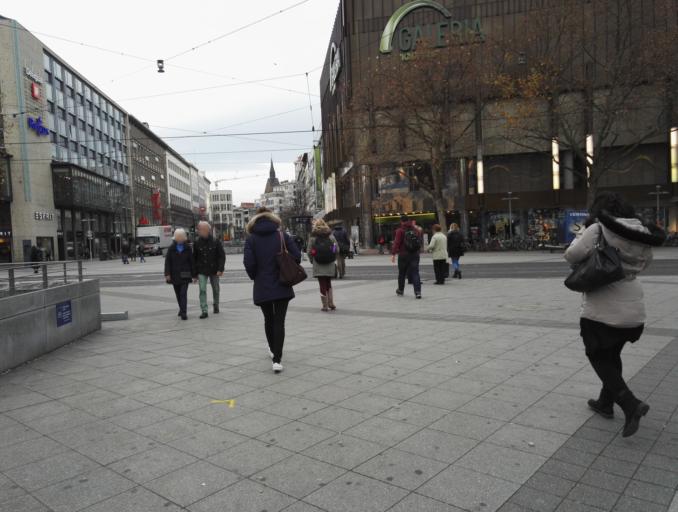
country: DE
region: Lower Saxony
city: Hannover
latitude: 52.3761
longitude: 9.7404
